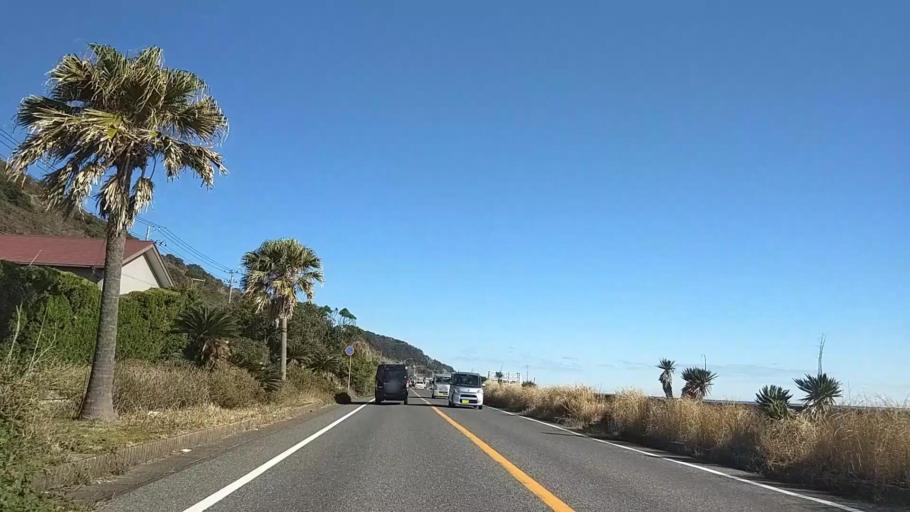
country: JP
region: Chiba
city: Kawaguchi
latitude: 35.0308
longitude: 140.0016
